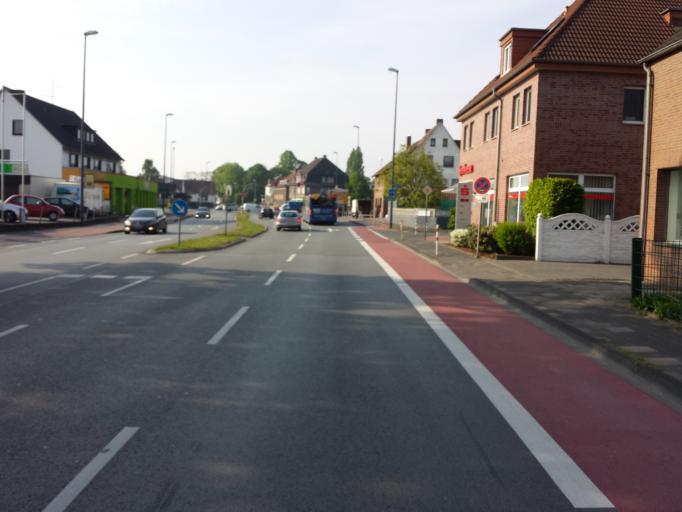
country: DE
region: North Rhine-Westphalia
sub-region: Regierungsbezirk Detmold
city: Guetersloh
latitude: 51.9153
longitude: 8.3718
